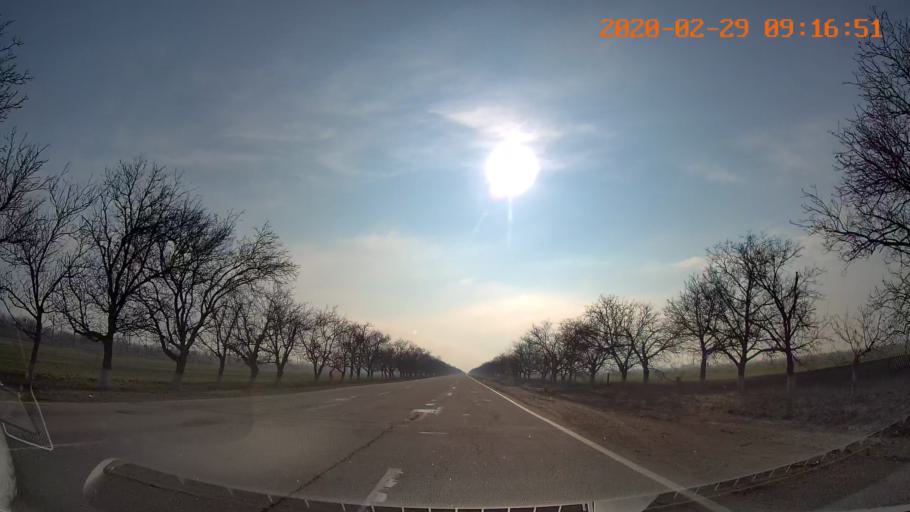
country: MD
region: Telenesti
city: Pervomaisc
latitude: 46.7882
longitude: 29.8938
